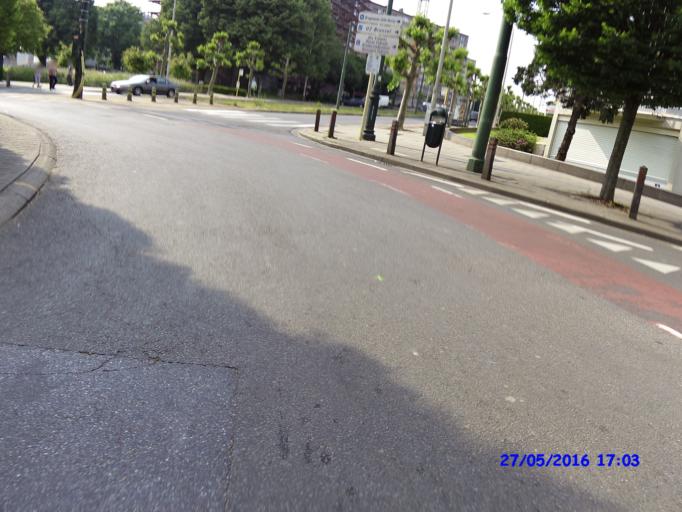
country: BE
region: Brussels Capital
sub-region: Bruxelles-Capitale
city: Brussels
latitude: 50.8831
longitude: 4.3358
